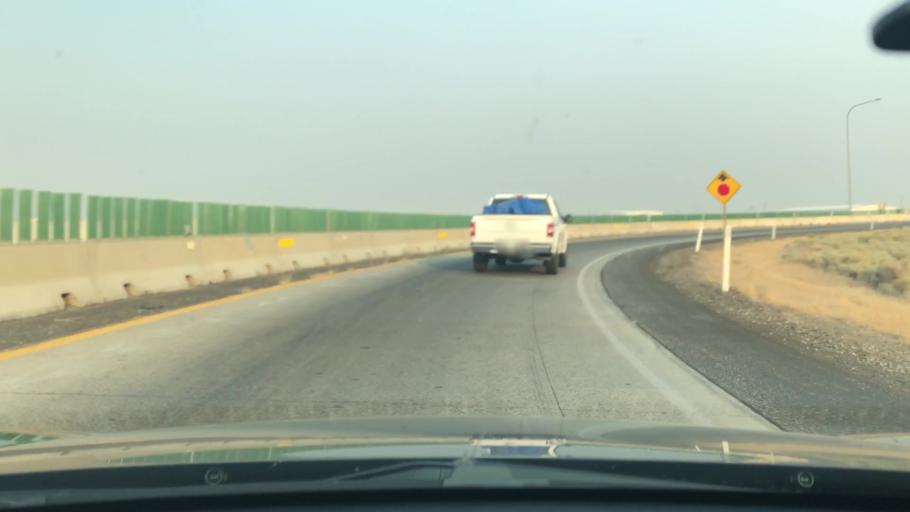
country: US
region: Washington
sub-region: Franklin County
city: Pasco
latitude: 46.2667
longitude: -119.0844
